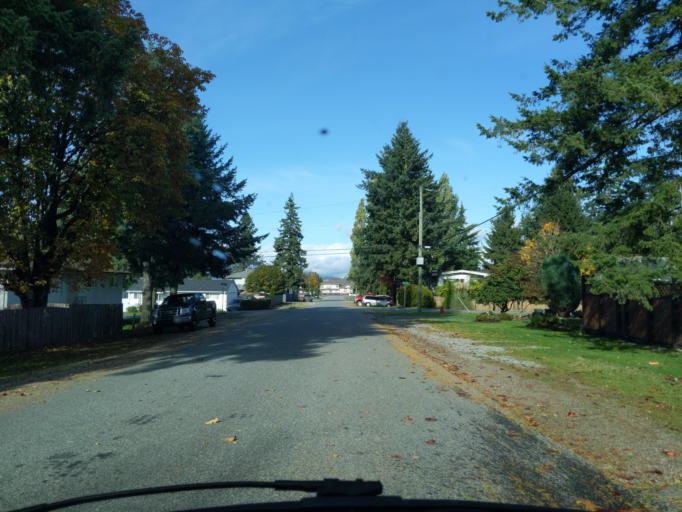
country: CA
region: British Columbia
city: New Westminster
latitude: 49.1965
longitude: -122.8624
